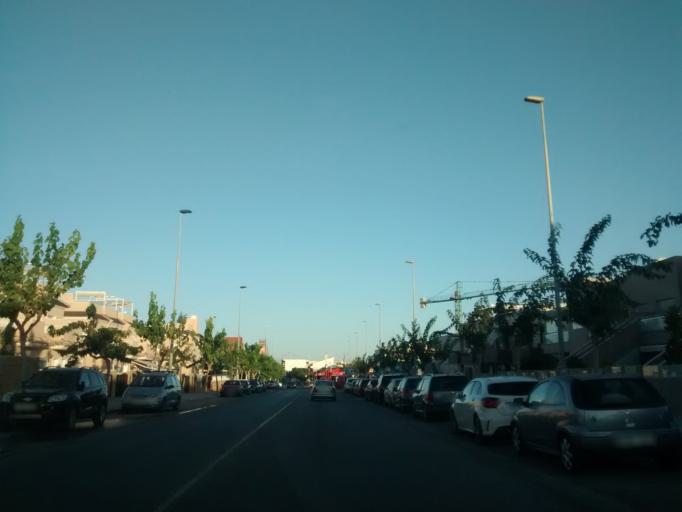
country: ES
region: Valencia
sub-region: Provincia de Alicante
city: Pilar de la Horadada
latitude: 37.8702
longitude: -0.7634
